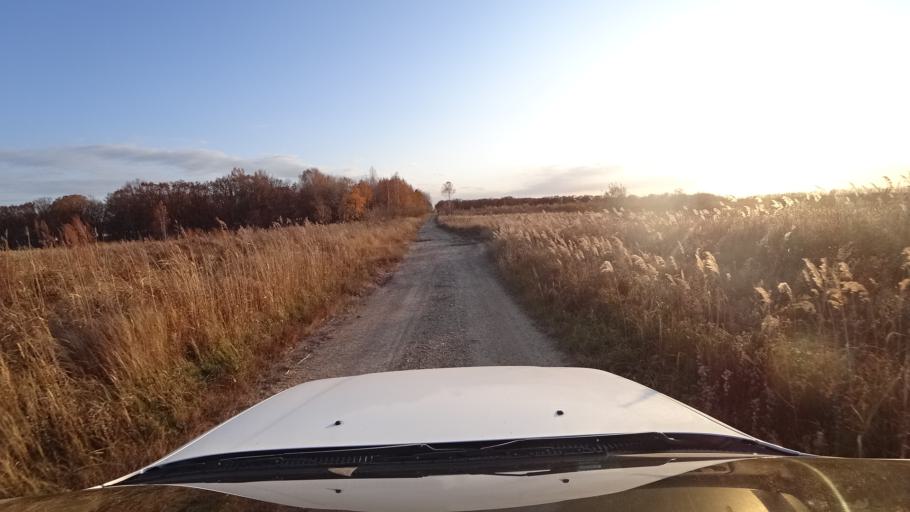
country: RU
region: Primorskiy
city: Lazo
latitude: 45.8079
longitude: 133.6064
